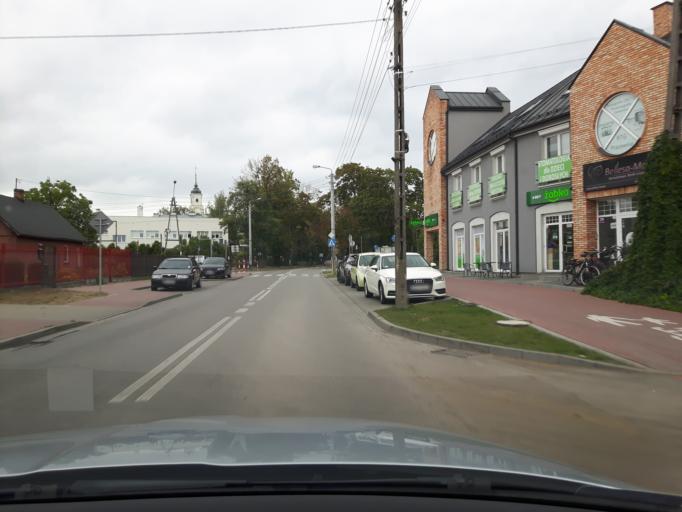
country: PL
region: Masovian Voivodeship
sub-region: Powiat wolominski
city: Kobylka
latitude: 52.3375
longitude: 21.1953
